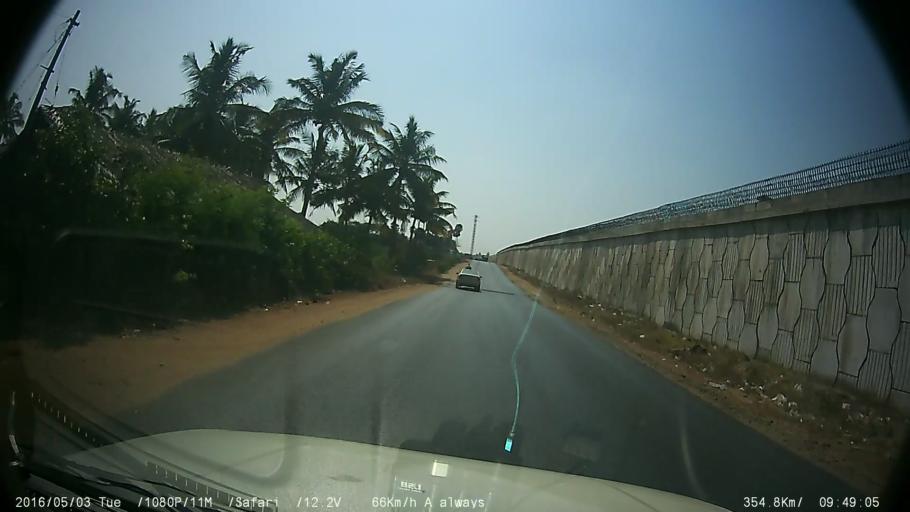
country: IN
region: Tamil Nadu
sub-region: Coimbatore
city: Madukkarai
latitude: 10.8722
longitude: 76.8935
